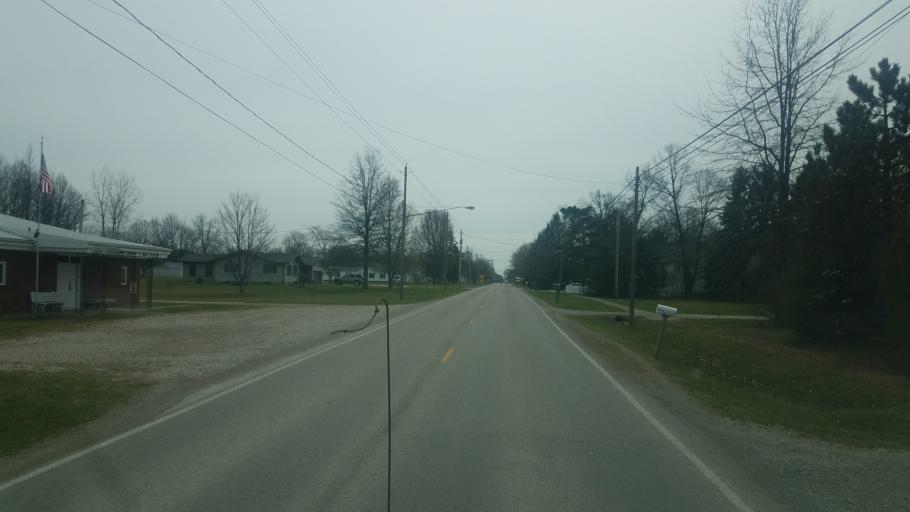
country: US
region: Ohio
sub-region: Huron County
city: Wakeman
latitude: 41.2523
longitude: -82.4916
